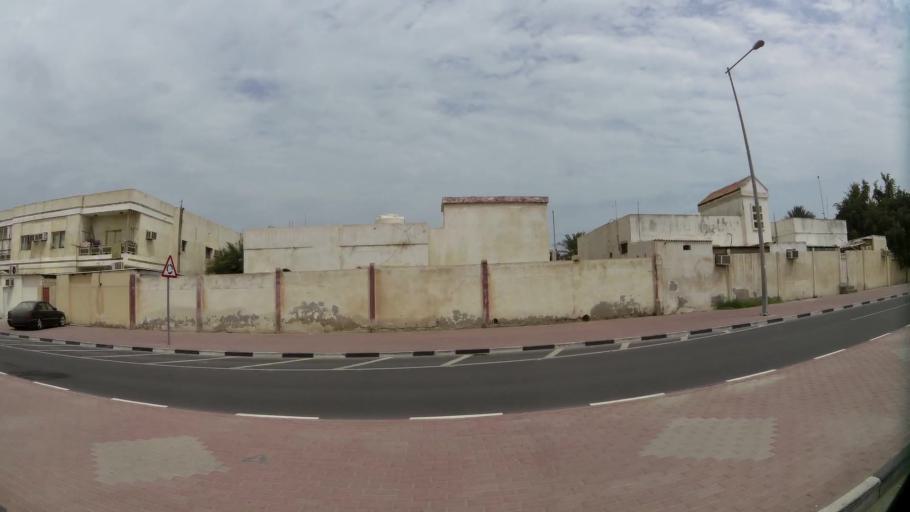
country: QA
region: Baladiyat ar Rayyan
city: Ar Rayyan
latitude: 25.3310
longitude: 51.4705
